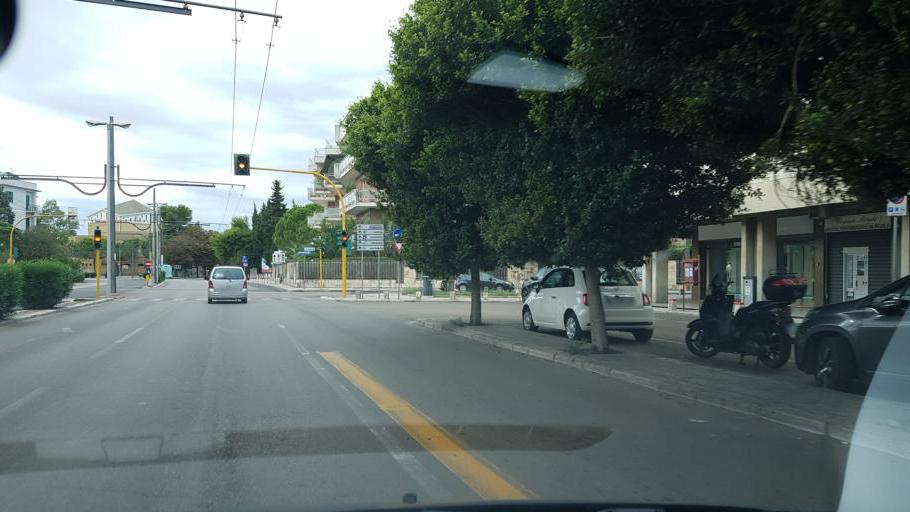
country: IT
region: Apulia
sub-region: Provincia di Lecce
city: Lecce
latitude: 40.3626
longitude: 18.1760
